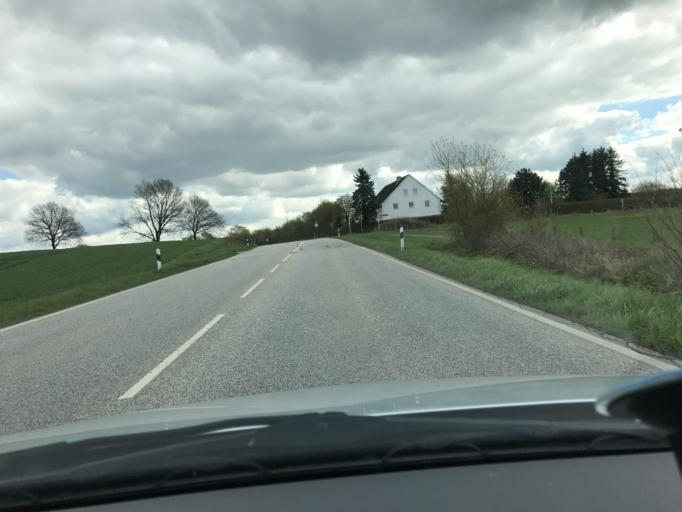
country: DE
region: Schleswig-Holstein
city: Bosdorf
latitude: 54.1340
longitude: 10.5036
